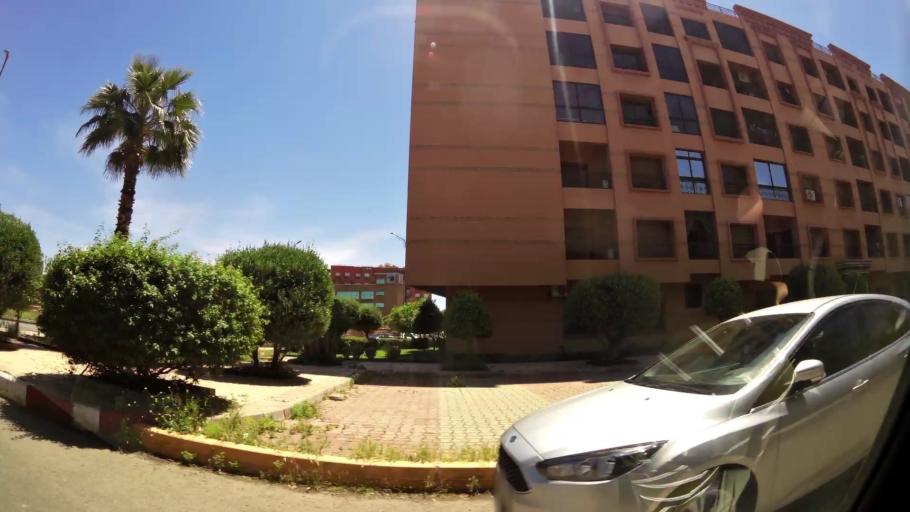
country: MA
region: Marrakech-Tensift-Al Haouz
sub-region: Marrakech
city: Marrakesh
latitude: 31.6216
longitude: -8.0135
